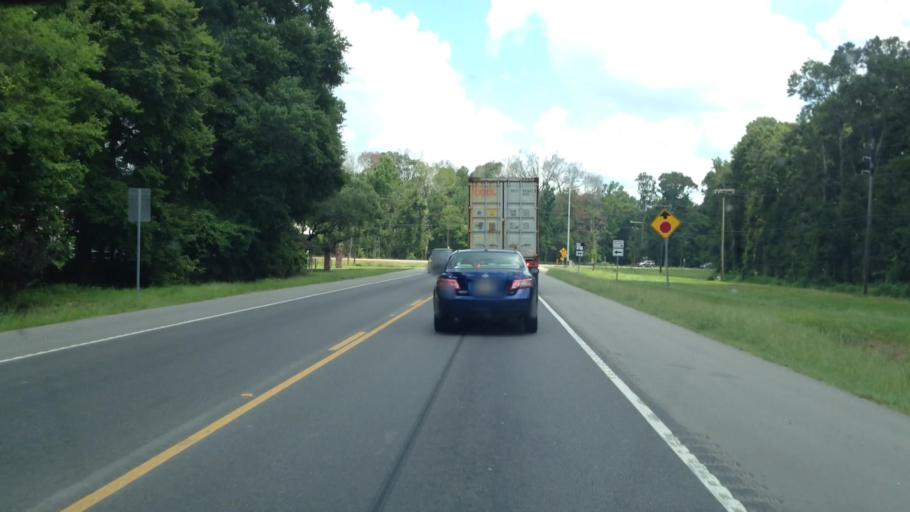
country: US
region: Louisiana
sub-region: Ascension Parish
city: Sorrento
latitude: 30.1649
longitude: -90.8803
